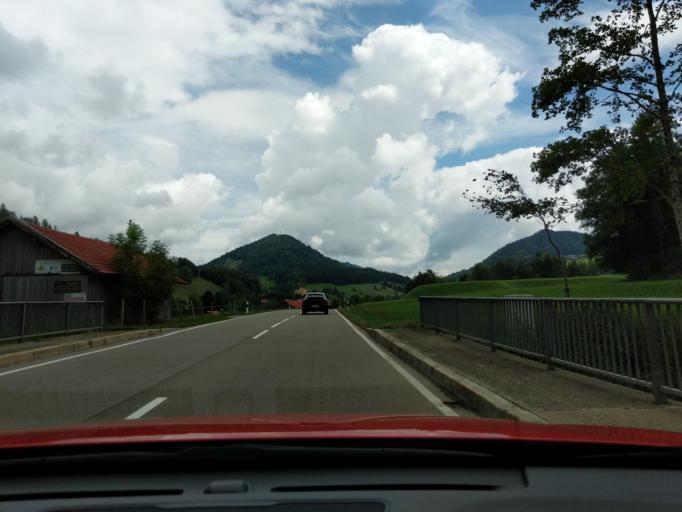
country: DE
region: Bavaria
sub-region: Swabia
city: Oberstaufen
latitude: 47.5390
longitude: 10.0060
